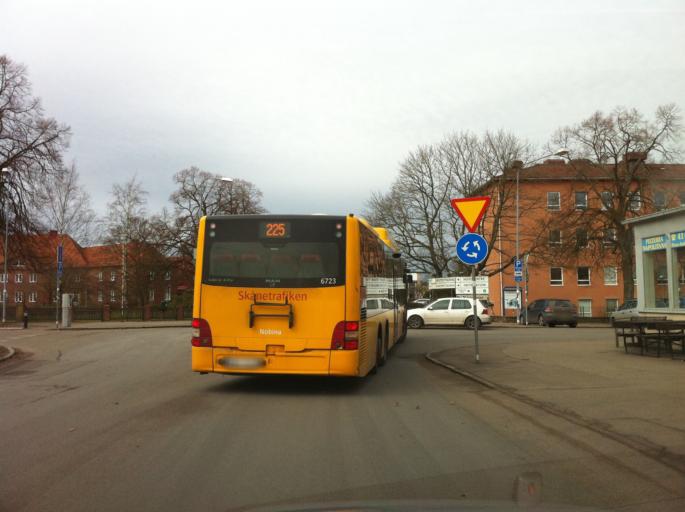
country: SE
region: Skane
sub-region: Angelholms Kommun
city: AEngelholm
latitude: 56.2380
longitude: 12.8609
